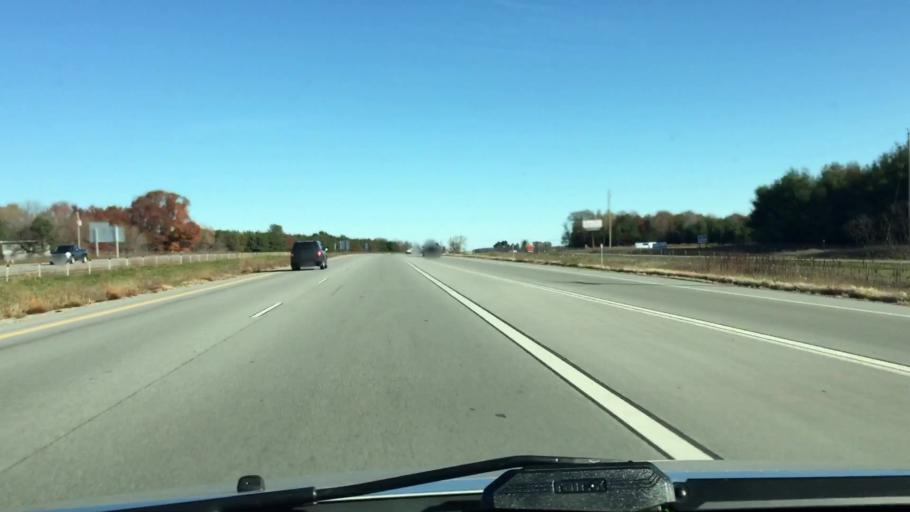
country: US
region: Wisconsin
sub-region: Brown County
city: Wrightstown
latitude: 44.3891
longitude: -88.1607
